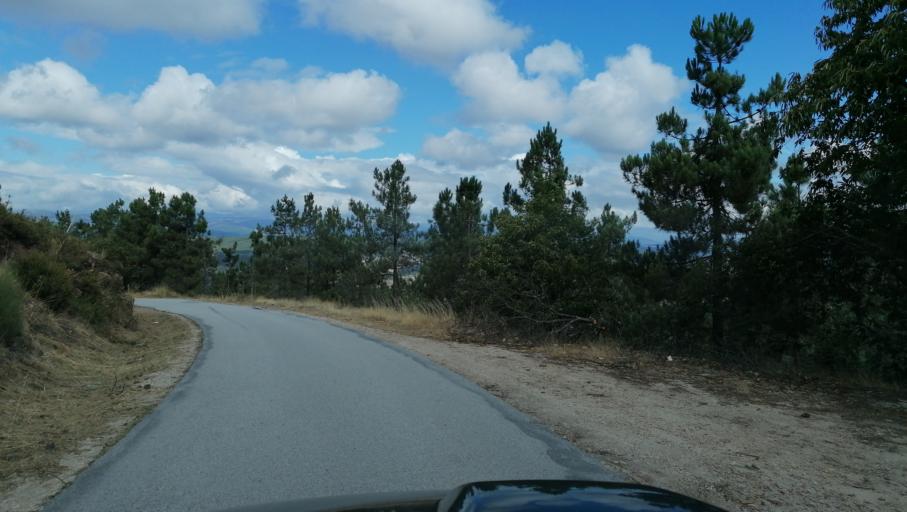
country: PT
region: Vila Real
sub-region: Vila Pouca de Aguiar
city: Vila Pouca de Aguiar
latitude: 41.5299
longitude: -7.5923
